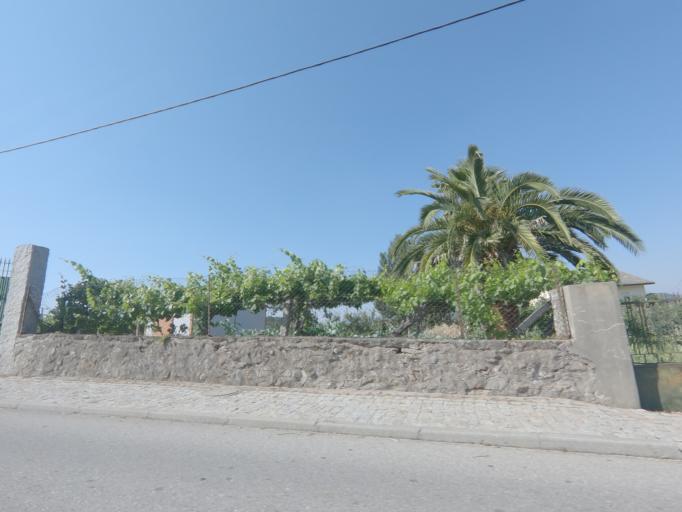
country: PT
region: Viseu
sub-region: Moimenta da Beira
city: Moimenta da Beira
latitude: 40.9809
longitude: -7.6095
